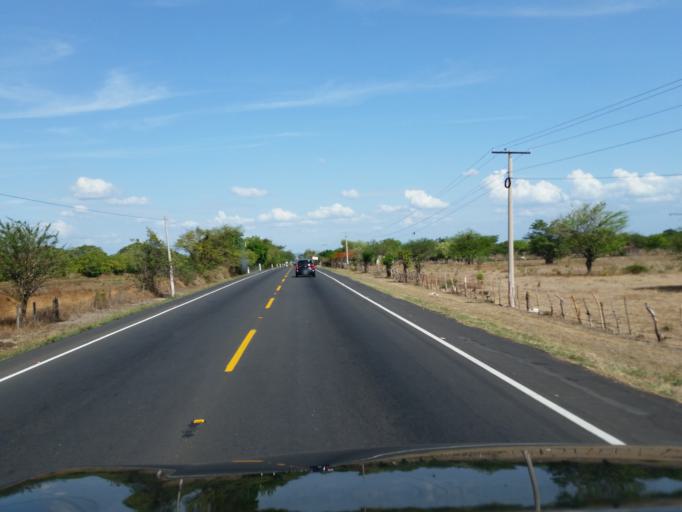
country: NI
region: Leon
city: La Paz Centro
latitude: 12.3190
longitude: -86.7929
